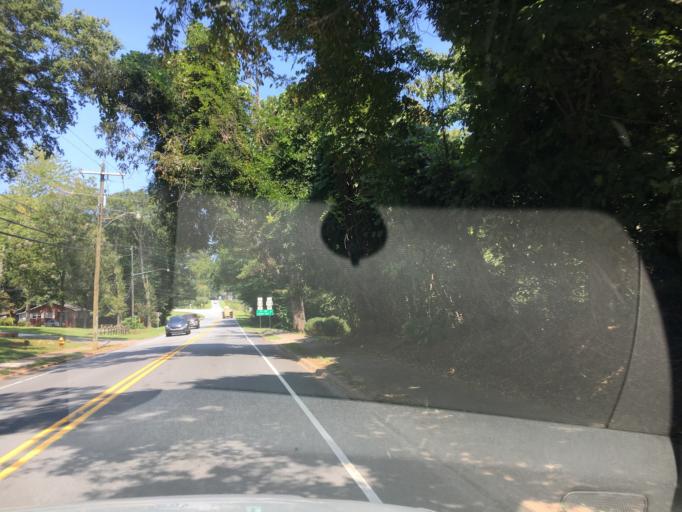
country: US
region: North Carolina
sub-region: Rutherford County
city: Rutherfordton
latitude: 35.3784
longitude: -81.9560
